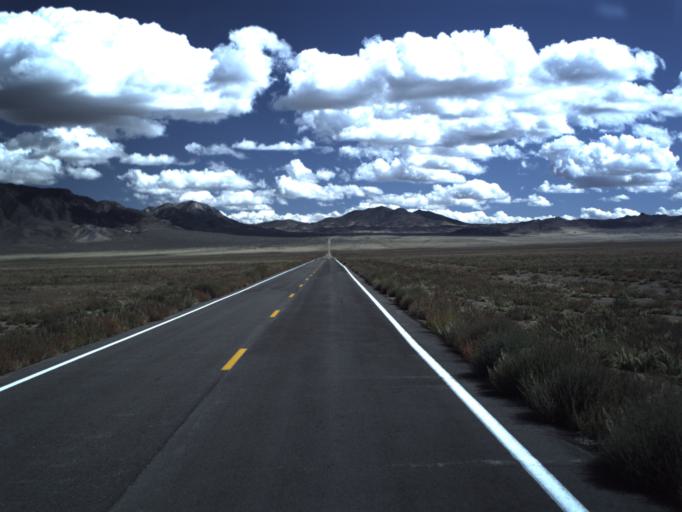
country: US
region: Utah
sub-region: Beaver County
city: Milford
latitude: 38.4725
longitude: -113.4131
